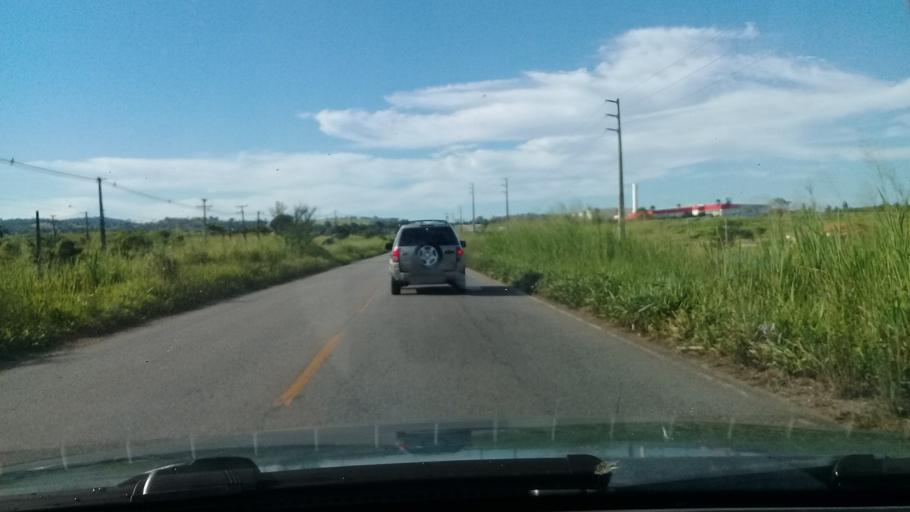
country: BR
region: Pernambuco
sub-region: Vitoria De Santo Antao
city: Vitoria de Santo Antao
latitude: -8.1070
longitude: -35.2619
